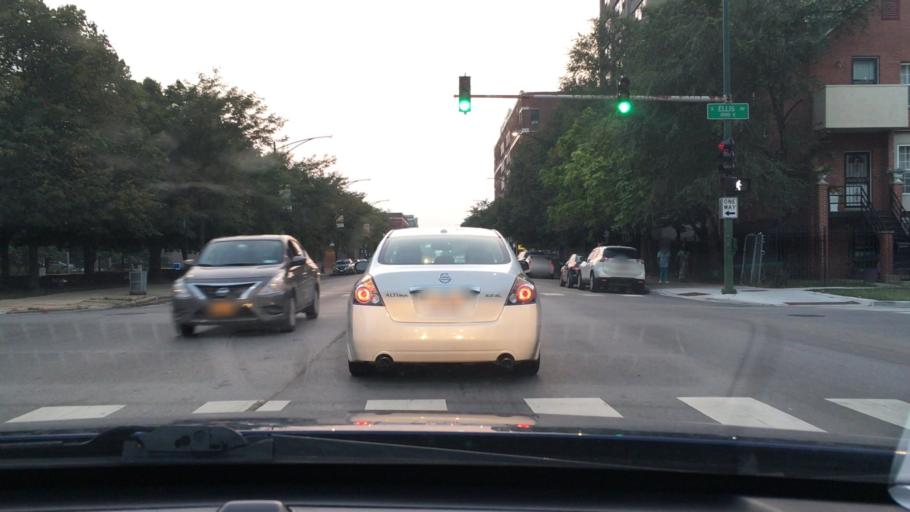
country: US
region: Illinois
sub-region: Cook County
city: Chicago
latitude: 41.8096
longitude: -87.6015
